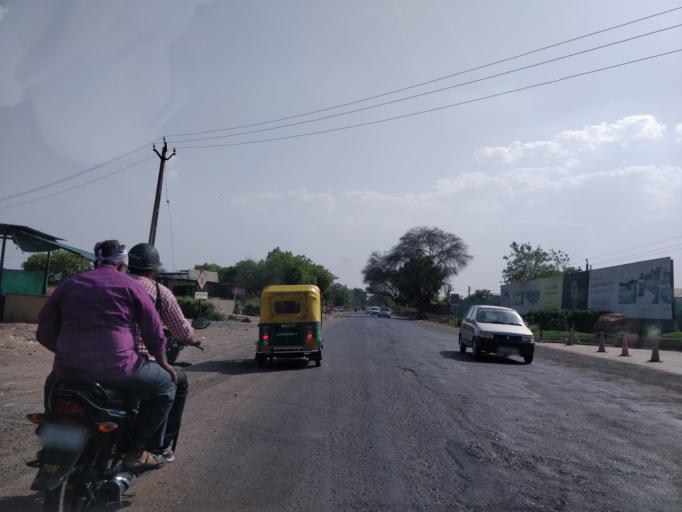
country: IN
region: Gujarat
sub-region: Ahmadabad
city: Naroda
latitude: 23.0995
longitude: 72.7031
